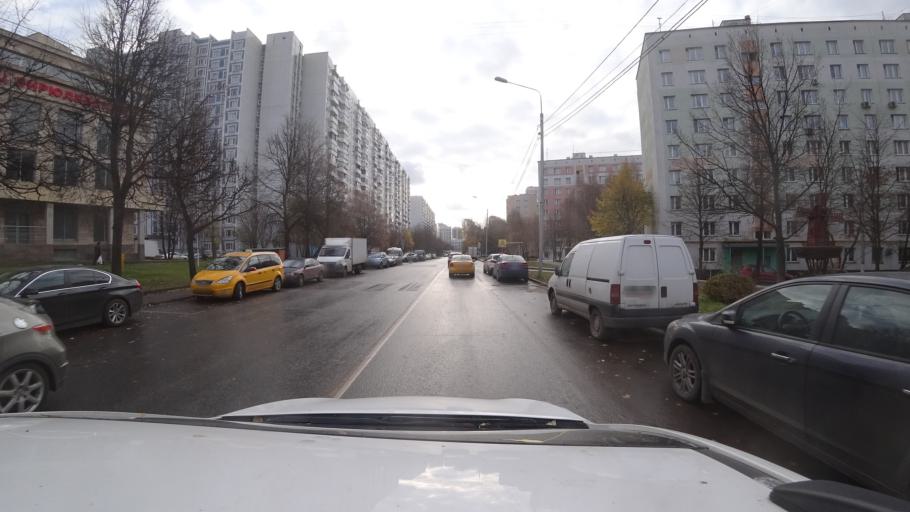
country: RU
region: Moscow
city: Zagor'ye
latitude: 55.5866
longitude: 37.6658
